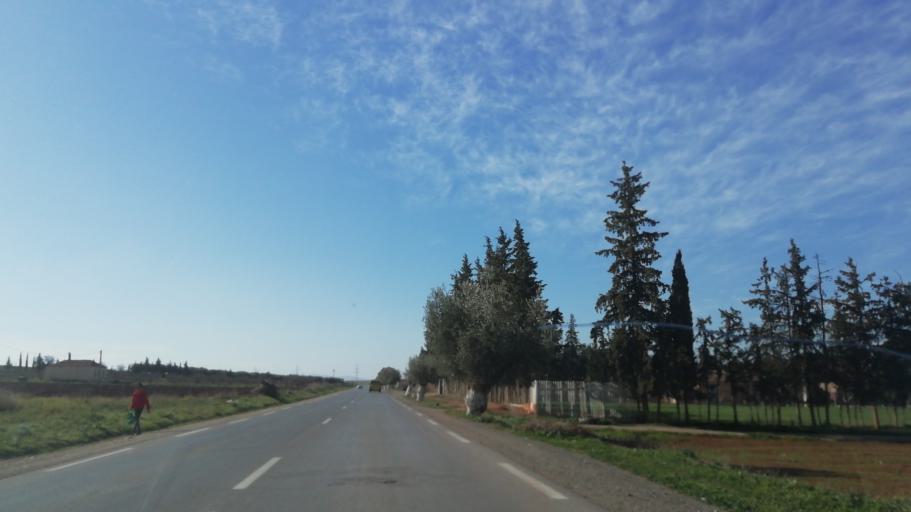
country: DZ
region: Tlemcen
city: Ouled Mimoun
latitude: 35.0223
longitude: -0.8984
